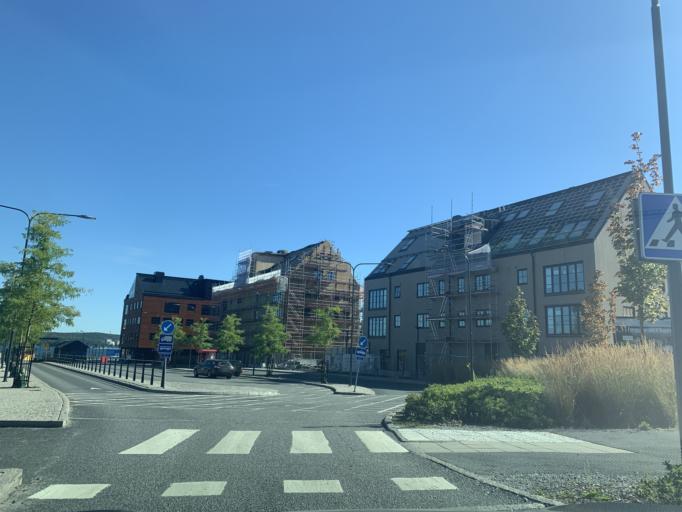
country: SE
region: Stockholm
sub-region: Botkyrka Kommun
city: Fittja
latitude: 59.2721
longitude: 17.8440
